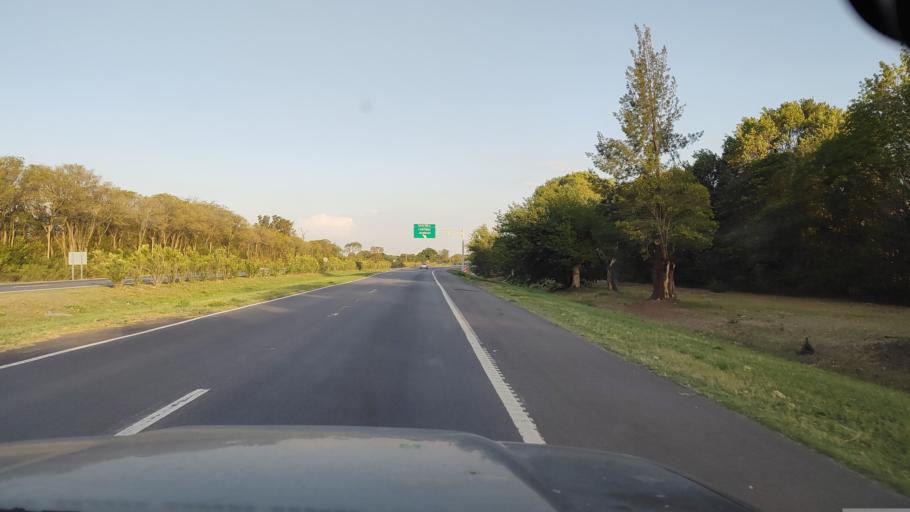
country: AR
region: Buenos Aires
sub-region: Partido de Lujan
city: Lujan
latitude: -34.5471
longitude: -59.2036
